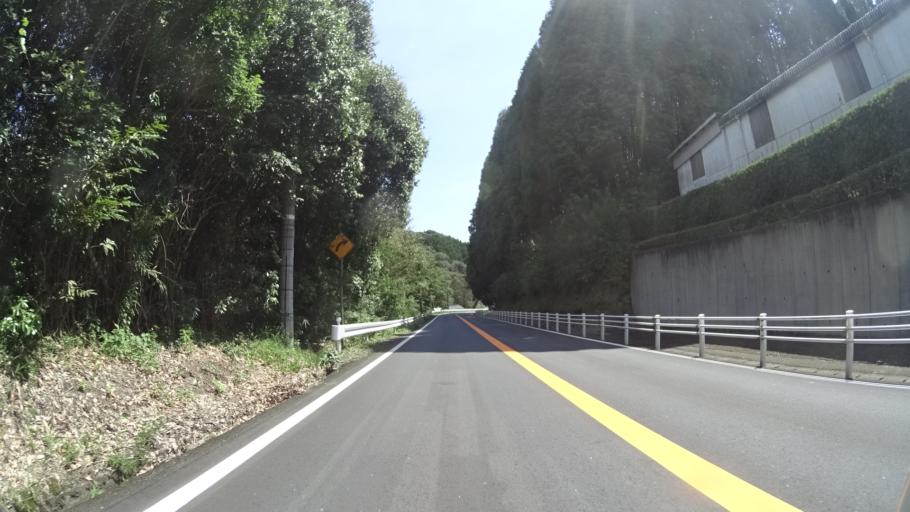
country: JP
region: Kagoshima
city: Kokubu-matsuki
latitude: 31.8480
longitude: 130.7523
